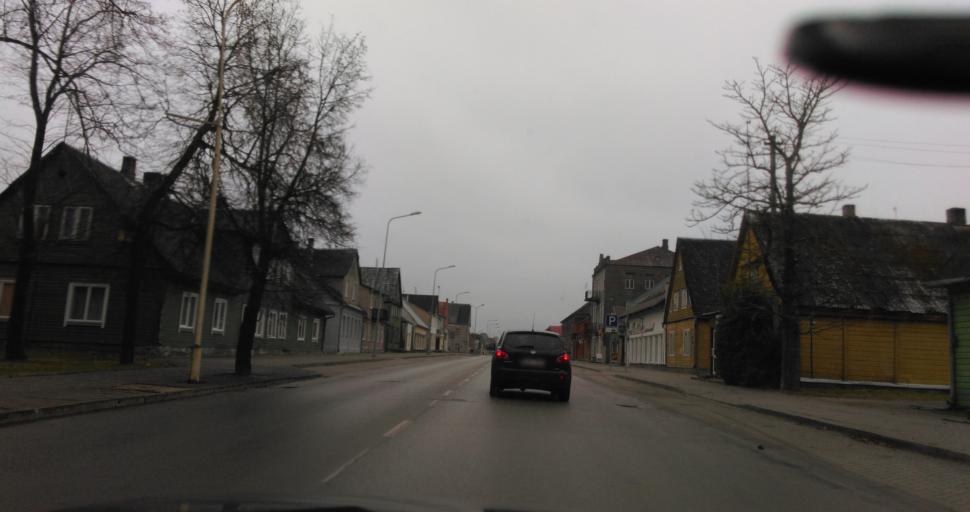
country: LT
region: Panevezys
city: Rokiskis
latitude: 55.9661
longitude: 25.5860
